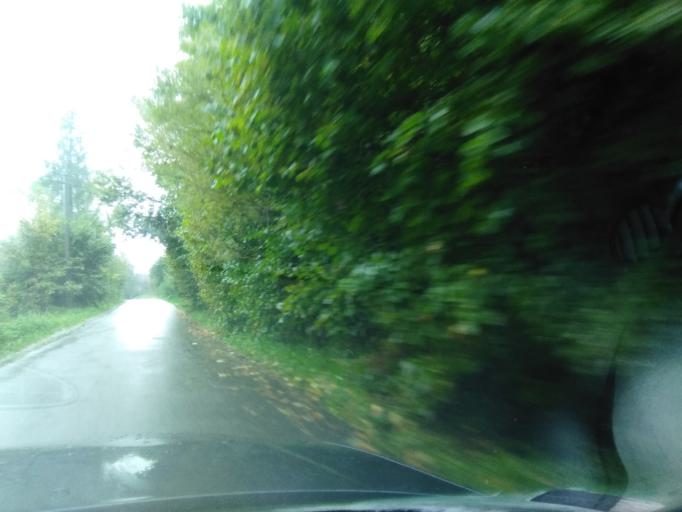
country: PL
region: Subcarpathian Voivodeship
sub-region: Powiat ropczycko-sedziszowski
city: Niedzwiada
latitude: 50.0093
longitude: 21.5491
